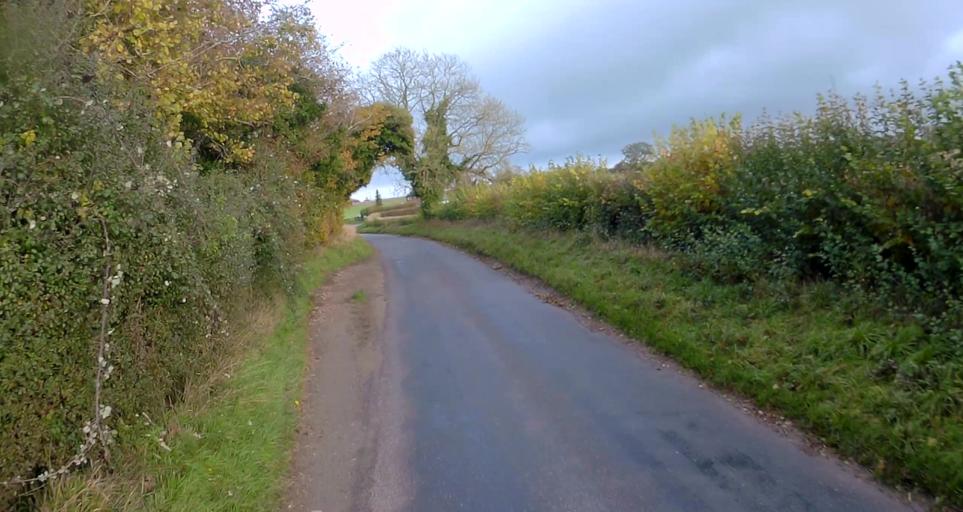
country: GB
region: England
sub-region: Hampshire
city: Four Marks
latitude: 51.1333
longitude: -1.1229
